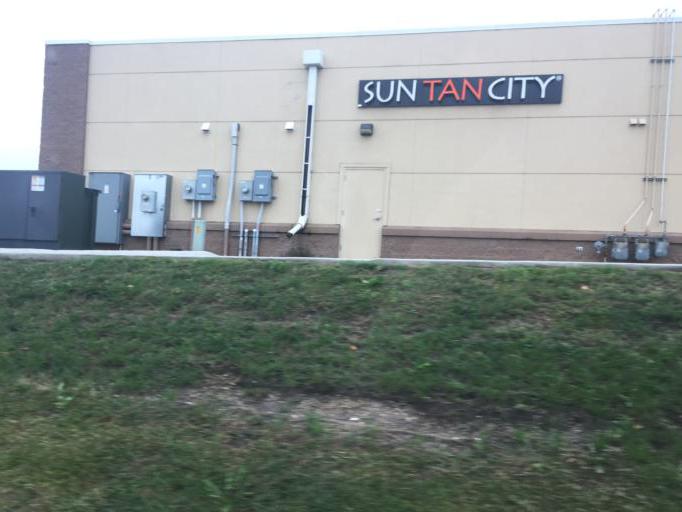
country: US
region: Minnesota
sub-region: Winona County
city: Winona
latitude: 44.0349
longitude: -91.6162
